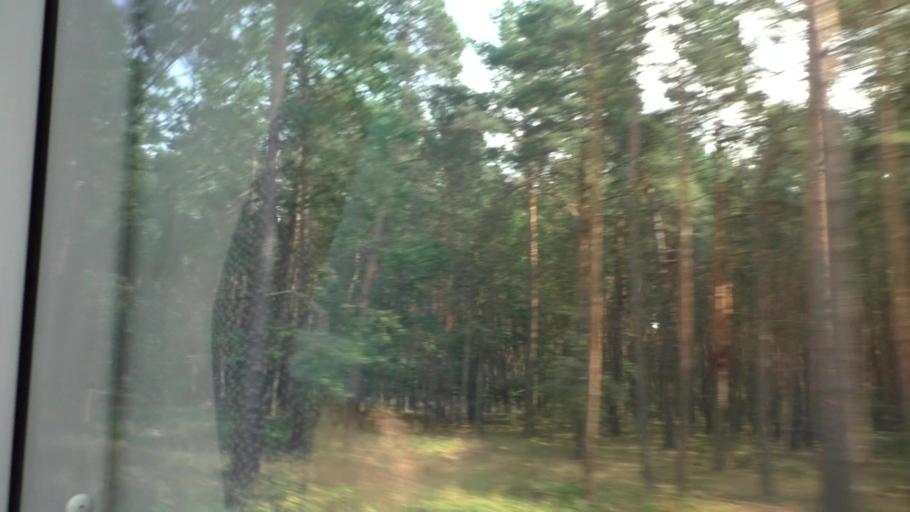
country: DE
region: Brandenburg
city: Wendisch Rietz
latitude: 52.1943
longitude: 14.0528
